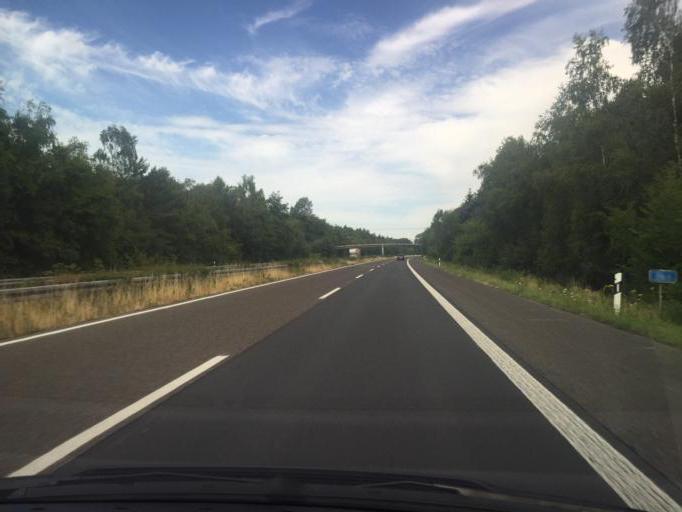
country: DE
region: North Rhine-Westphalia
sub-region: Regierungsbezirk Dusseldorf
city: Sonsbeck
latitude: 51.5899
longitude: 6.3767
